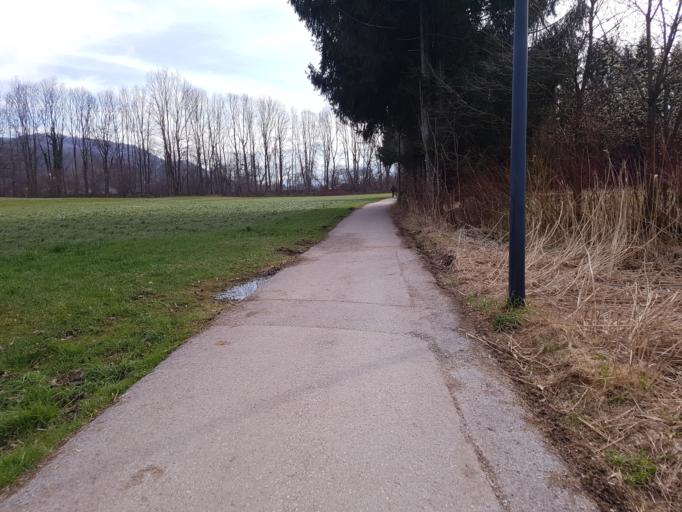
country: AT
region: Salzburg
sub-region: Politischer Bezirk Salzburg-Umgebung
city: Elsbethen
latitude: 47.7852
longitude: 13.0856
